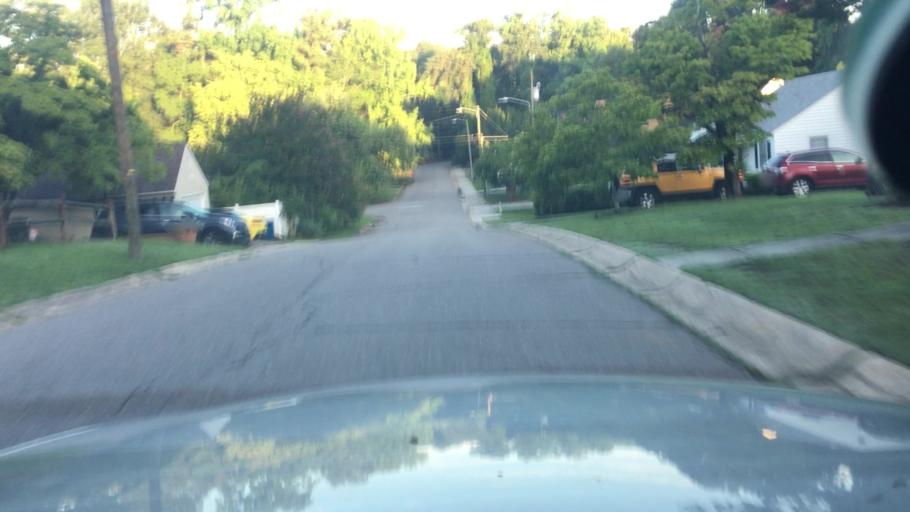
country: US
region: North Carolina
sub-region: Cumberland County
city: Fayetteville
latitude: 35.0679
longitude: -78.9118
